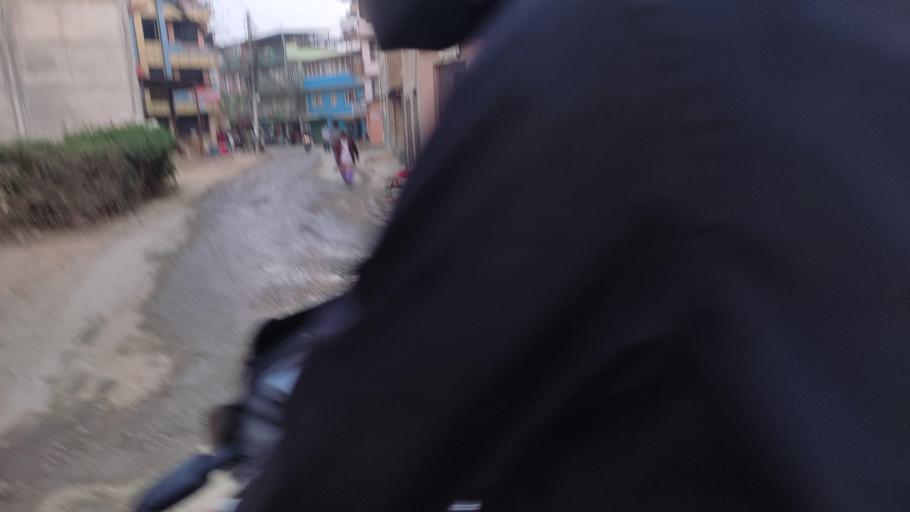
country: NP
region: Central Region
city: Kirtipur
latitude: 27.6705
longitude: 85.2805
